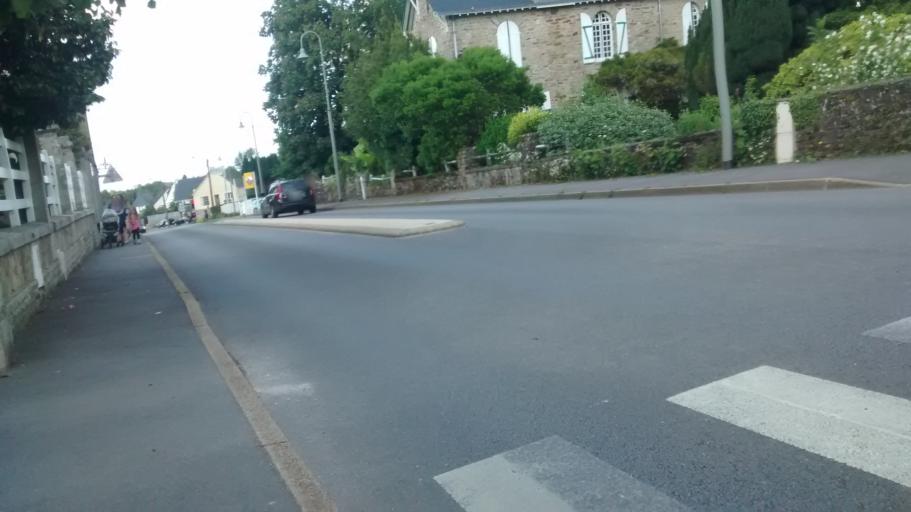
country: FR
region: Brittany
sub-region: Departement du Morbihan
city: Questembert
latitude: 47.6626
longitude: -2.4505
